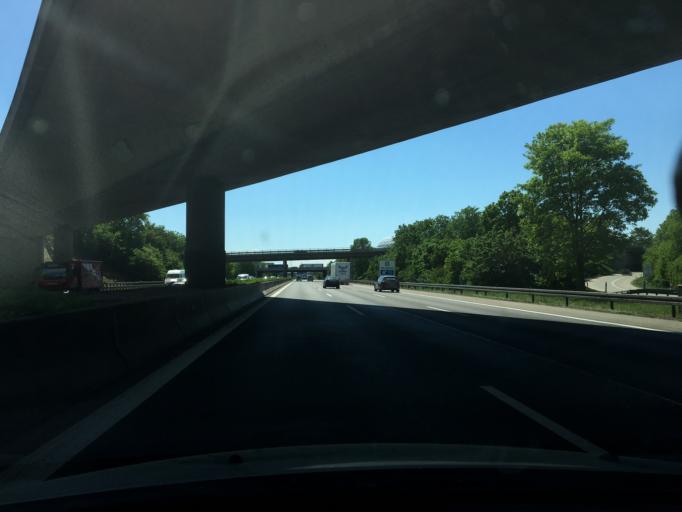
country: DE
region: Bavaria
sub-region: Upper Bavaria
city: Garching bei Munchen
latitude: 48.2247
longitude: 11.6310
